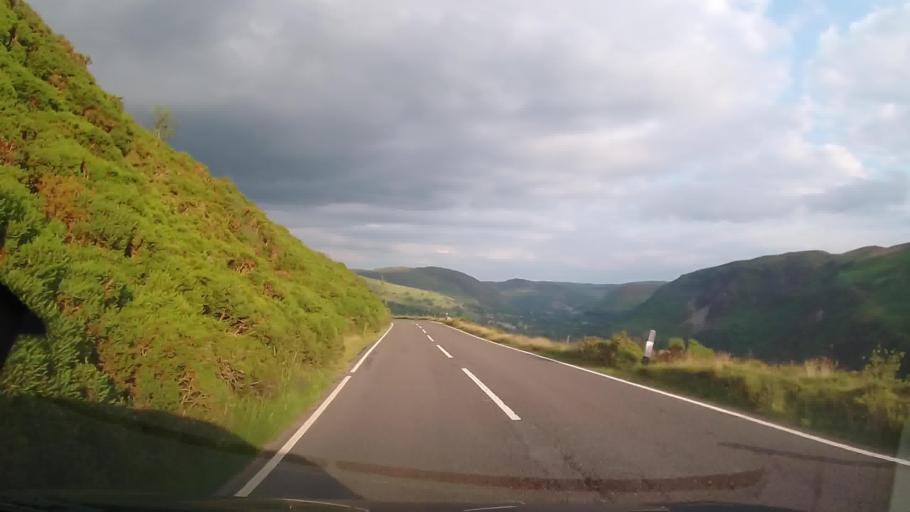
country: GB
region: Wales
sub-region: Sir Powys
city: Llangynog
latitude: 52.8560
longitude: -3.4495
